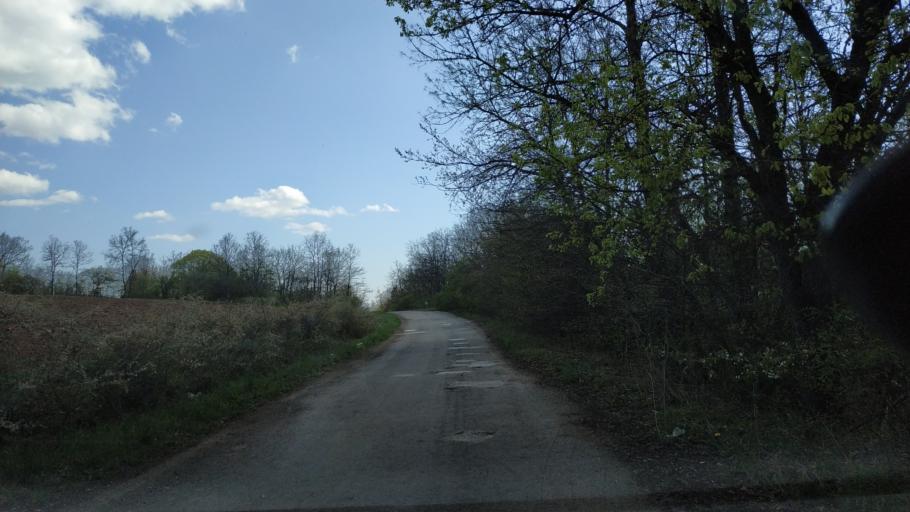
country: RS
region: Central Serbia
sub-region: Zajecarski Okrug
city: Soko Banja
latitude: 43.5567
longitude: 21.8930
